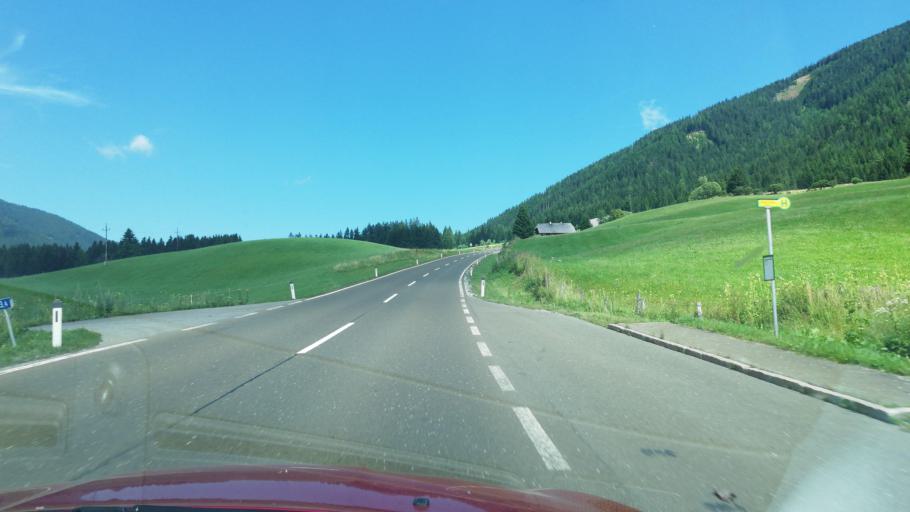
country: AT
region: Styria
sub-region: Politischer Bezirk Murtal
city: Hohentauern
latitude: 47.4036
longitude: 14.4633
